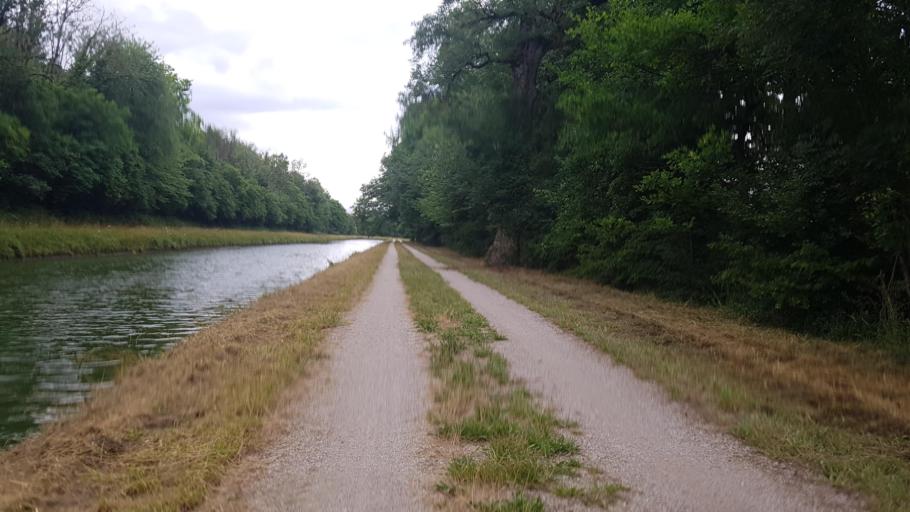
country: FR
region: Lorraine
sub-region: Departement de la Moselle
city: Lorquin
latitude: 48.6908
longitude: 6.9836
